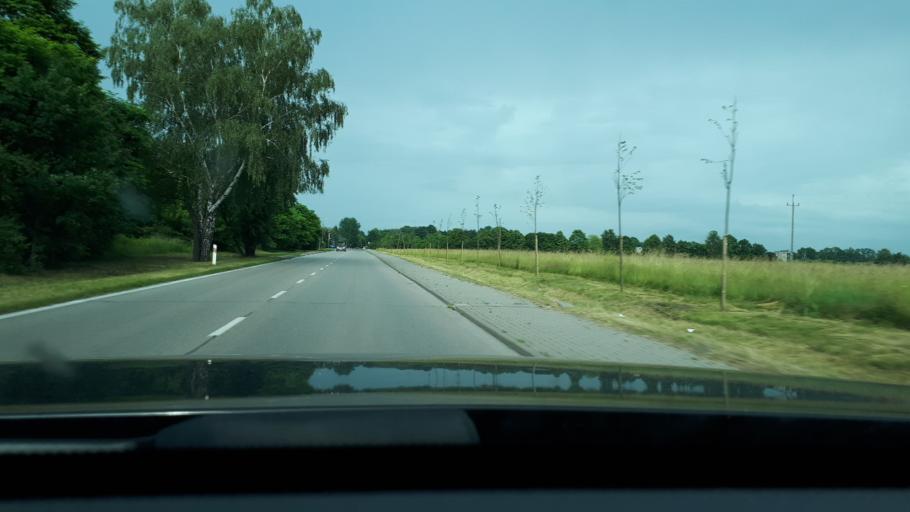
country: PL
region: Masovian Voivodeship
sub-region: Powiat warszawski zachodni
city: Leszno
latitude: 52.2624
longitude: 20.6386
